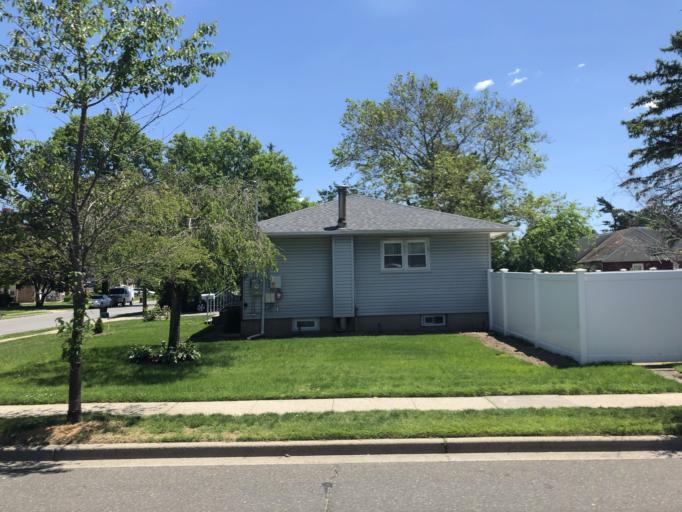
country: US
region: New York
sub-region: Nassau County
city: Uniondale
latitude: 40.6960
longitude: -73.5948
